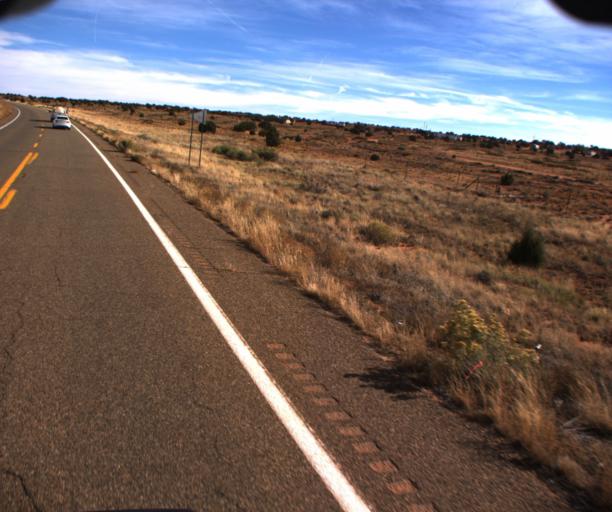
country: US
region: Arizona
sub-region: Coconino County
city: Kaibito
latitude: 36.5825
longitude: -111.1080
